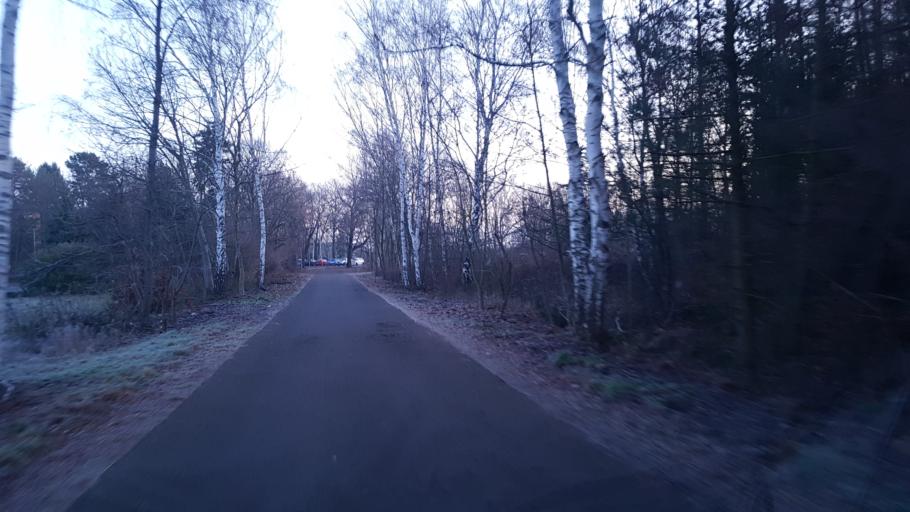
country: DE
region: Brandenburg
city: Schipkau
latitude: 51.5530
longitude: 13.8872
